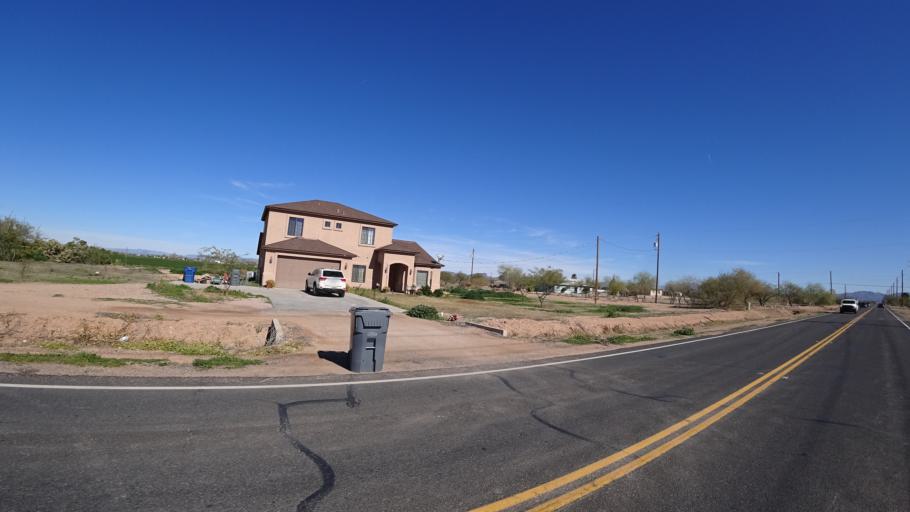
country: US
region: Arizona
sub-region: Maricopa County
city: Scottsdale
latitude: 33.4951
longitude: -111.8501
